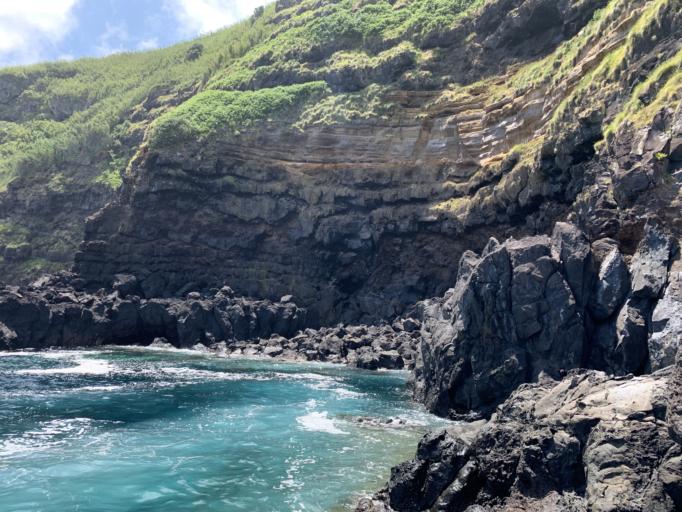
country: PT
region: Azores
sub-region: Ponta Delgada
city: Arrifes
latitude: 37.8993
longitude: -25.7494
